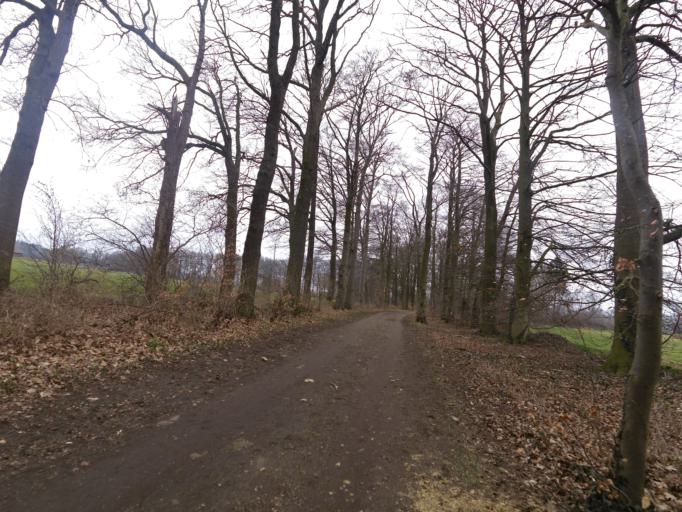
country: DE
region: North Rhine-Westphalia
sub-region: Regierungsbezirk Munster
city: Isselburg
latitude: 51.8638
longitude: 6.4286
